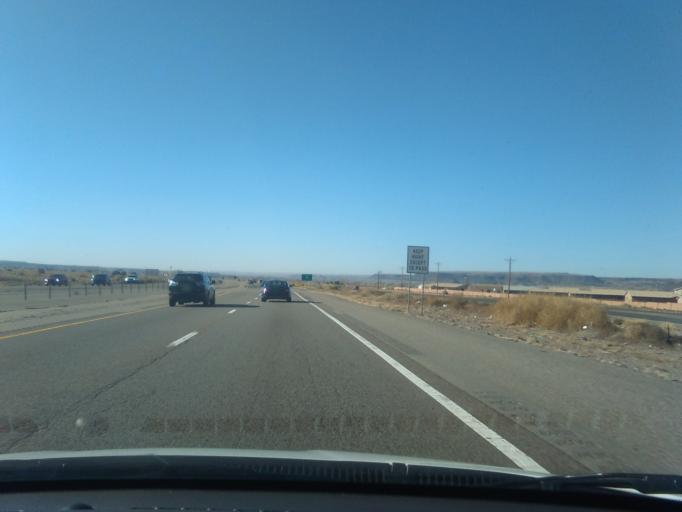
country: US
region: New Mexico
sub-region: Sandoval County
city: San Felipe Pueblo
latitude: 35.3982
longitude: -106.4427
